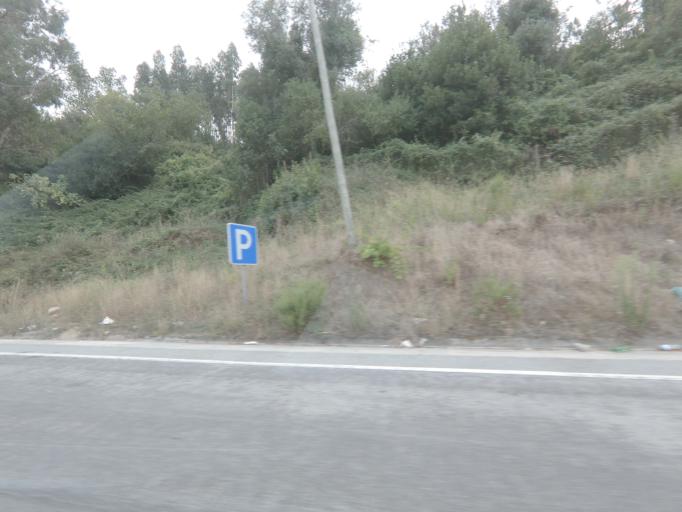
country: PT
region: Aveiro
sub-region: Mealhada
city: Pampilhosa do Botao
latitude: 40.3051
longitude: -8.4010
